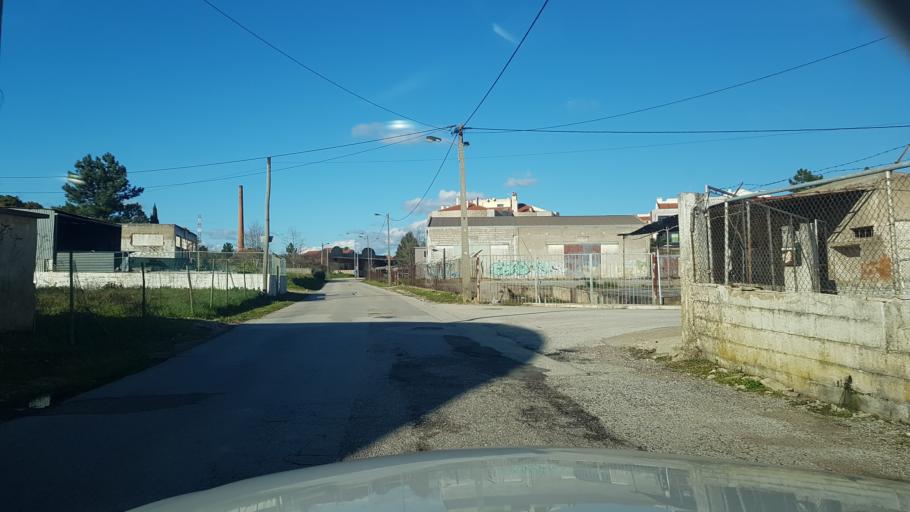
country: PT
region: Santarem
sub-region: Entroncamento
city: Entroncamento
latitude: 39.4759
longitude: -8.4735
